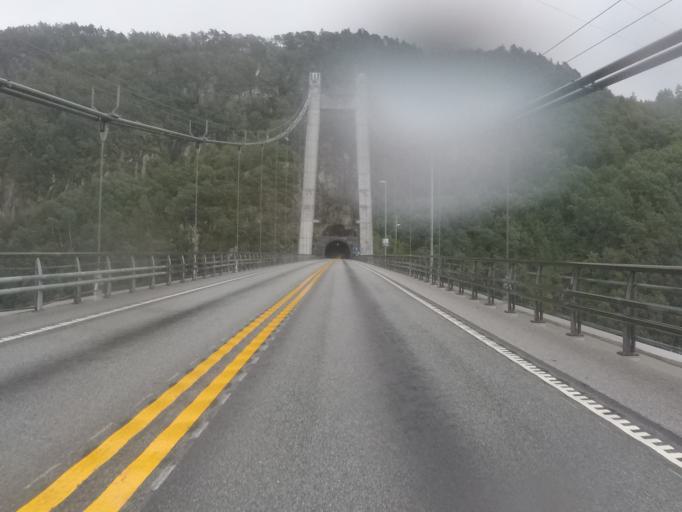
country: NO
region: Vest-Agder
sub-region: Kvinesdal
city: Liknes
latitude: 58.2611
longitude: 6.8458
